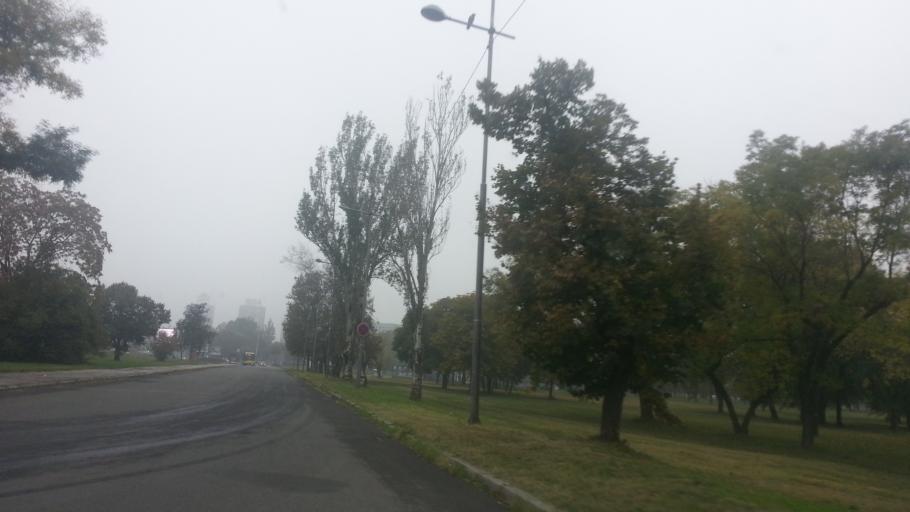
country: RS
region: Central Serbia
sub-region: Belgrade
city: Stari Grad
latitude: 44.8150
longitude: 20.4432
